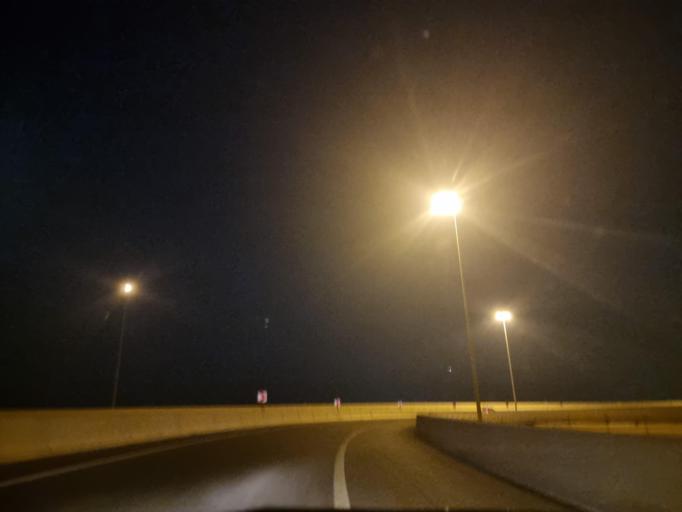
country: AE
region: Abu Dhabi
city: Abu Dhabi
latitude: 24.4185
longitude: 54.7653
